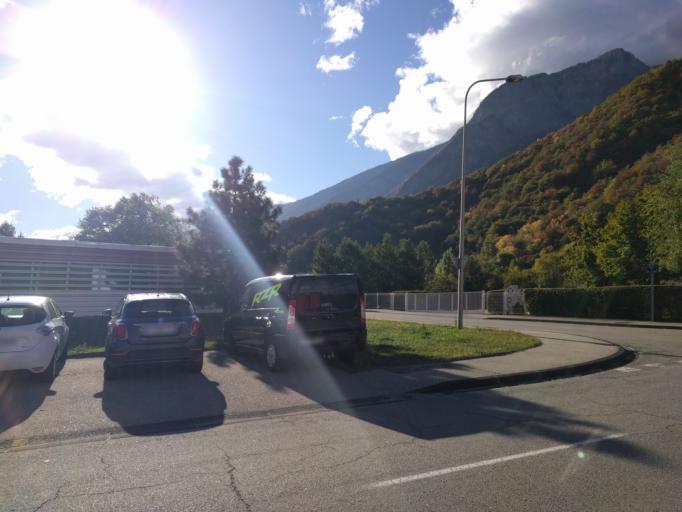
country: FR
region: Rhone-Alpes
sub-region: Departement de la Savoie
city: Villargondran
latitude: 45.2670
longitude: 6.3688
